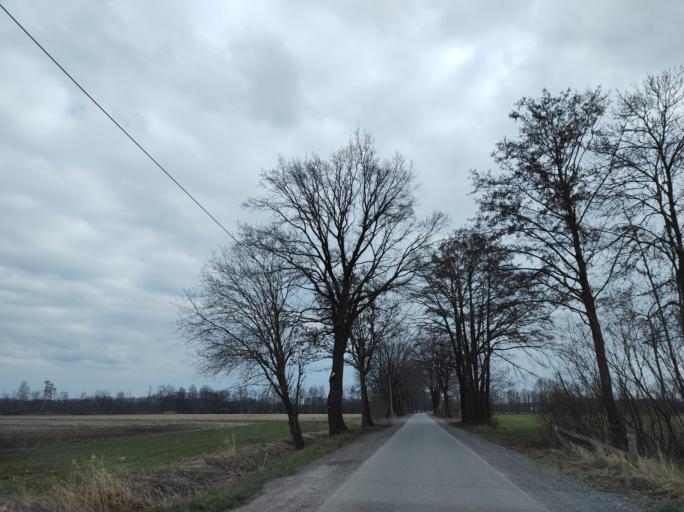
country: DE
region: North Rhine-Westphalia
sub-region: Regierungsbezirk Detmold
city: Delbruck
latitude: 51.7469
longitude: 8.5424
